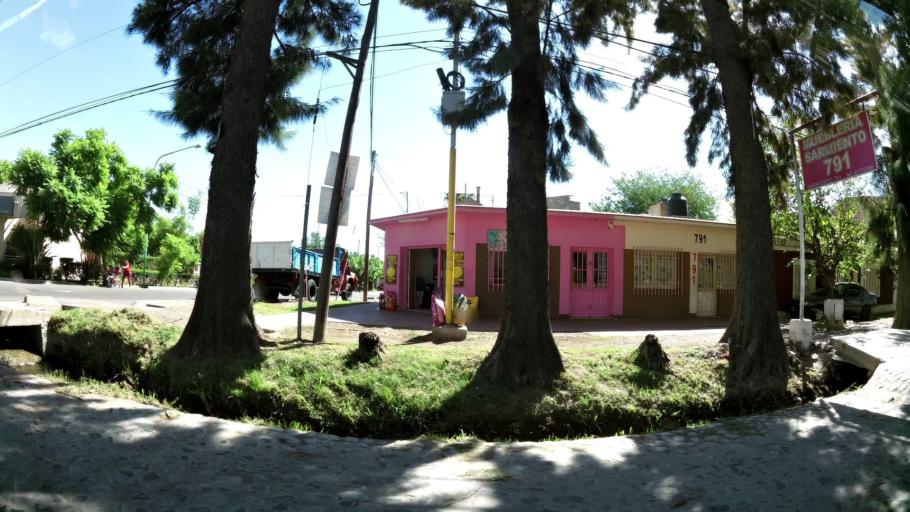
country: AR
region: Mendoza
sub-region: Departamento de Maipu
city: Maipu
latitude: -32.9487
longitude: -68.7942
